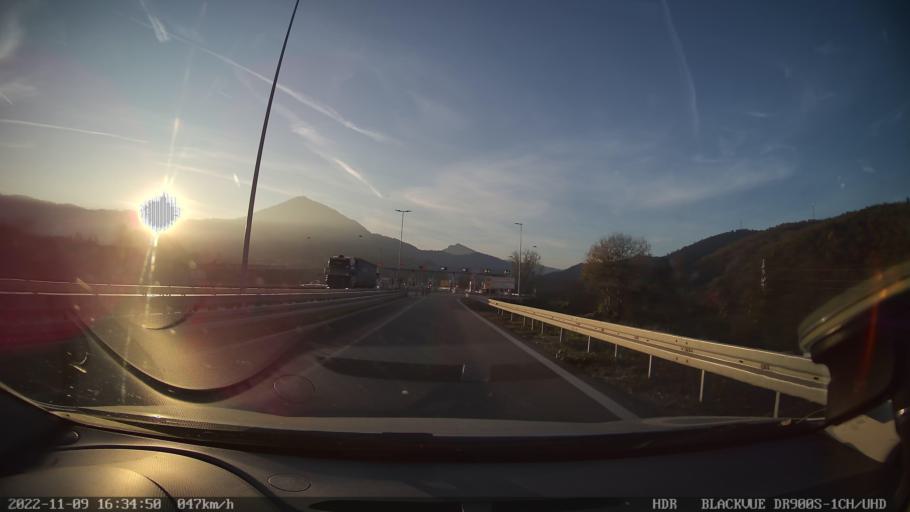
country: RS
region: Central Serbia
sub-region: Moravicki Okrug
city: Cacak
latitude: 43.9030
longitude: 20.2632
